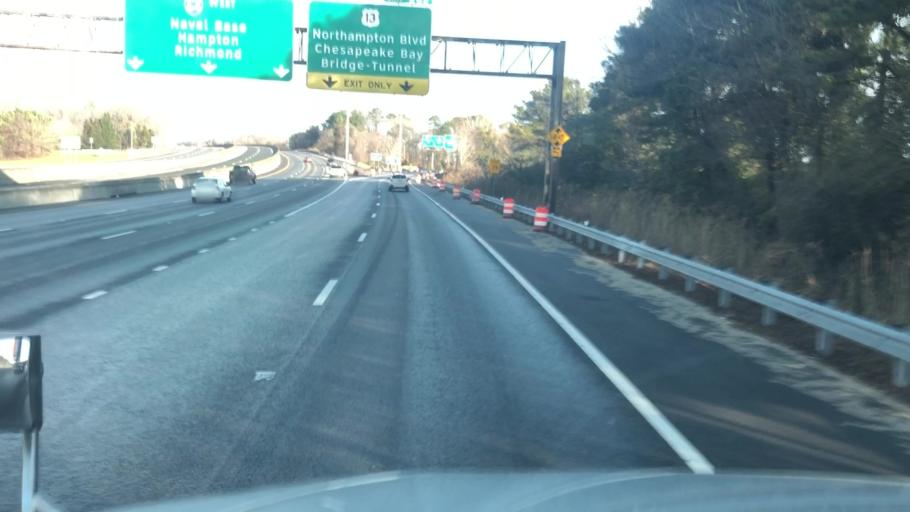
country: US
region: Virginia
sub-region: City of Norfolk
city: Norfolk
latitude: 36.8721
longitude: -76.1955
